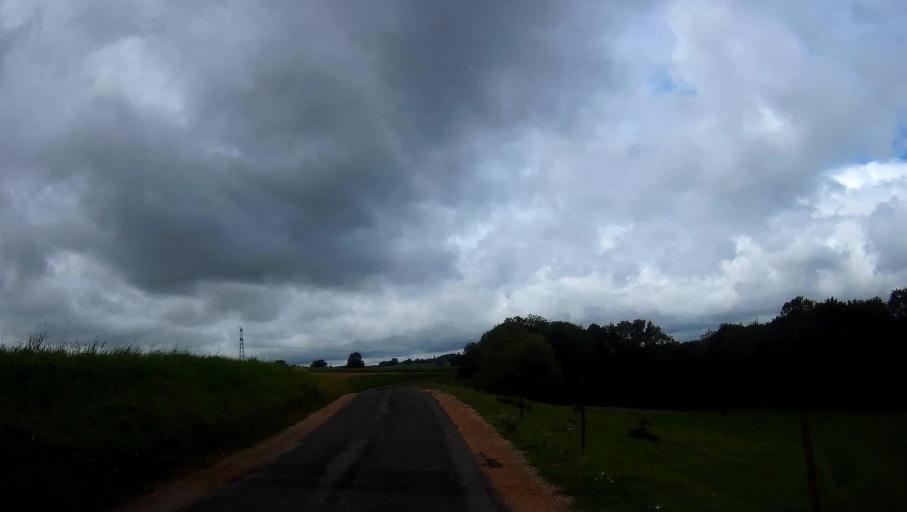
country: FR
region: Champagne-Ardenne
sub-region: Departement des Ardennes
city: Rimogne
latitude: 49.7571
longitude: 4.5335
